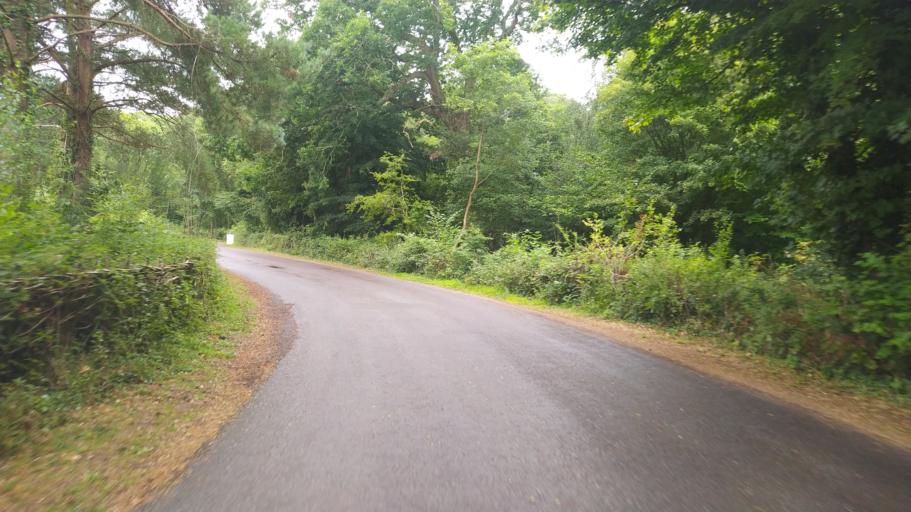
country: GB
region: England
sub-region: Hampshire
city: Hedge End
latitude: 50.8971
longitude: -1.2935
